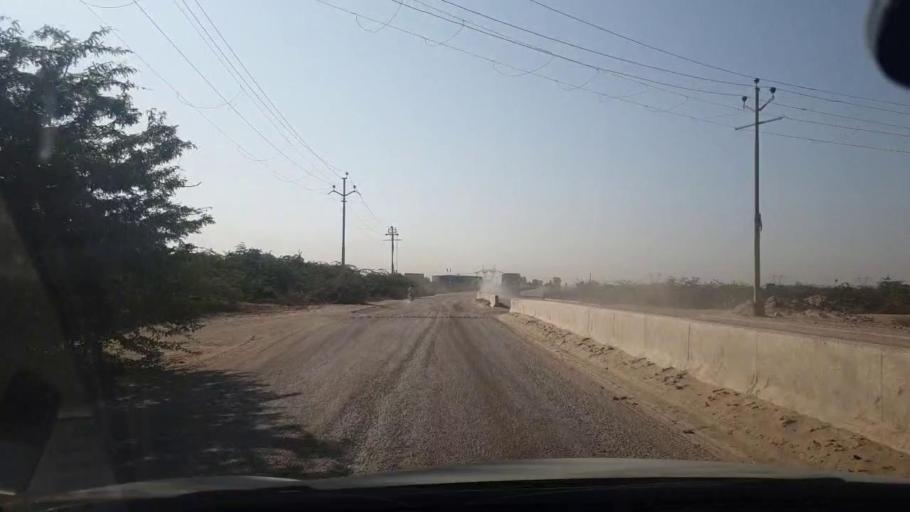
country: PK
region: Sindh
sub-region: Karachi District
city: Karachi
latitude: 25.0769
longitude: 67.0139
